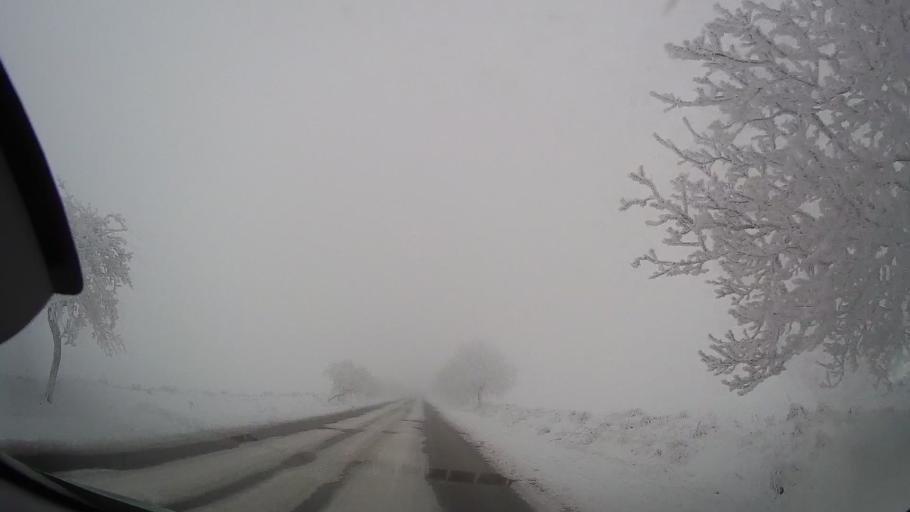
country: RO
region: Neamt
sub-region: Comuna Valea Ursului
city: Valea Ursului
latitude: 46.8189
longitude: 27.0646
